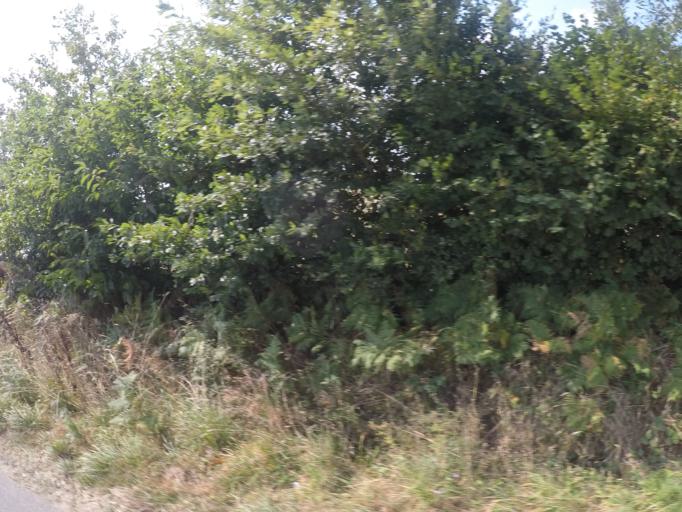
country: FR
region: Brittany
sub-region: Departement des Cotes-d'Armor
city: Tremuson
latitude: 48.5364
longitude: -2.8927
